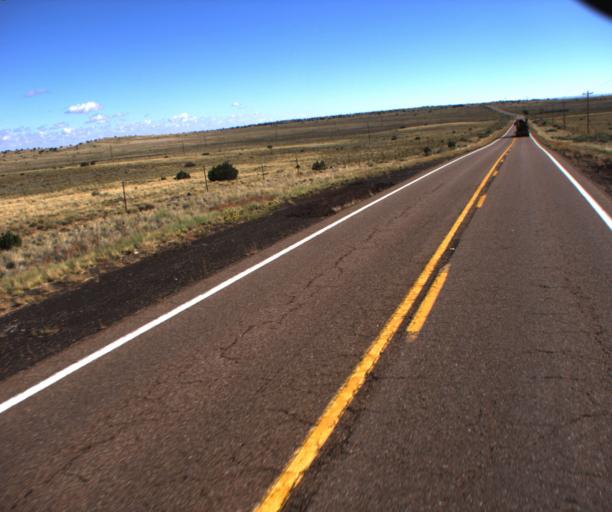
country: US
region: Arizona
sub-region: Apache County
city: Saint Johns
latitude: 34.4885
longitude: -109.5262
